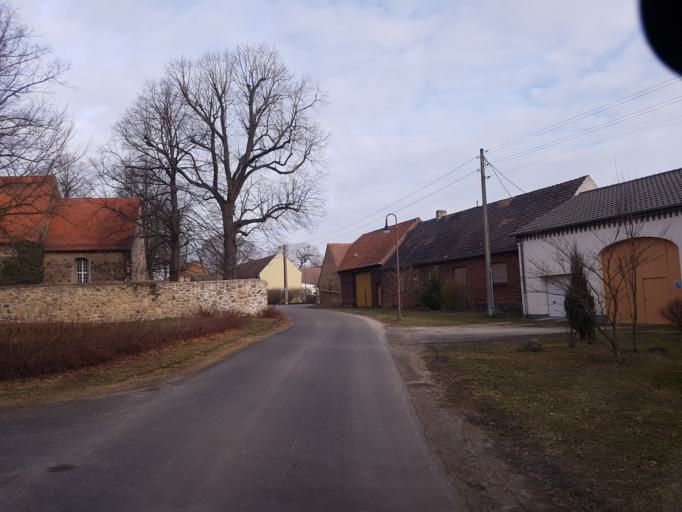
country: DE
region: Brandenburg
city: Finsterwalde
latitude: 51.6271
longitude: 13.7682
